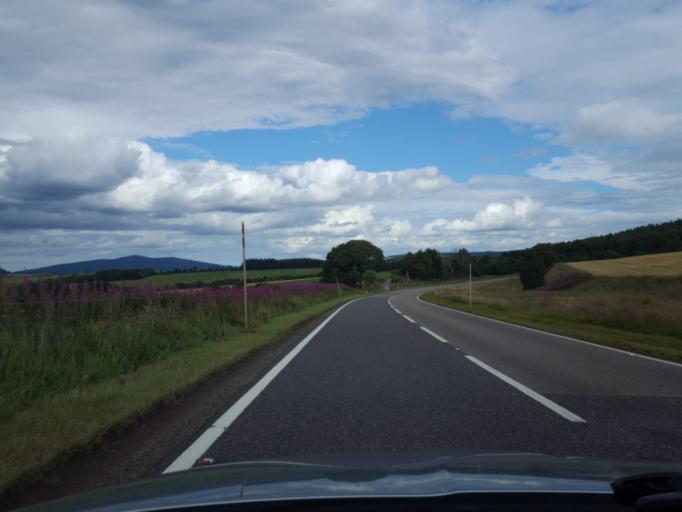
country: GB
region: Scotland
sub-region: Moray
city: Rothes
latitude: 57.4438
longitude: -3.2813
